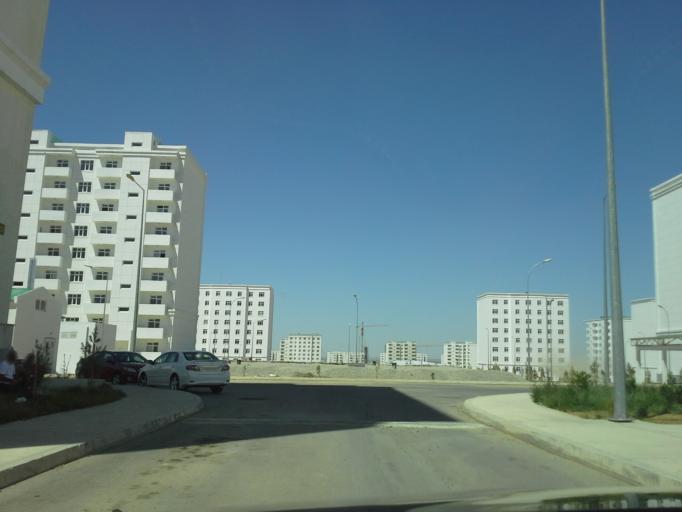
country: TM
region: Ahal
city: Ashgabat
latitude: 37.8886
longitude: 58.4112
